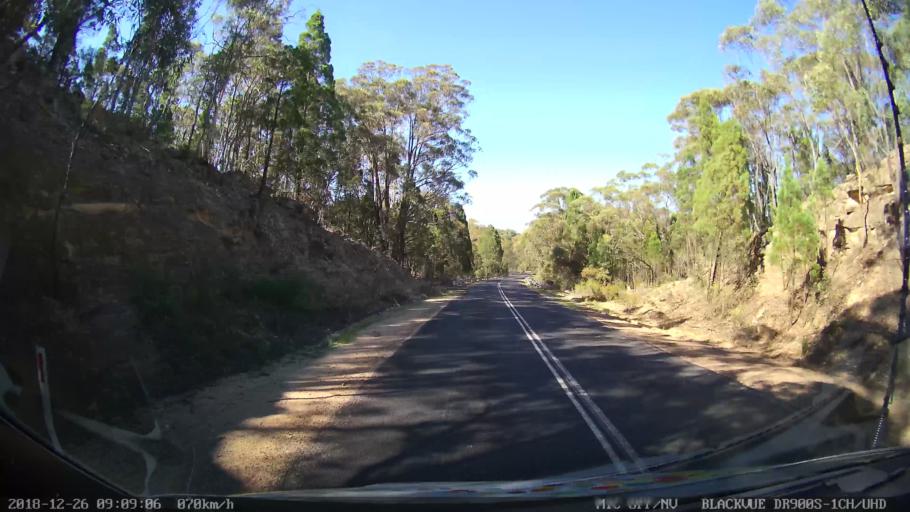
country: AU
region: New South Wales
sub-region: Mid-Western Regional
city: Kandos
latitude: -32.7217
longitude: 149.9988
